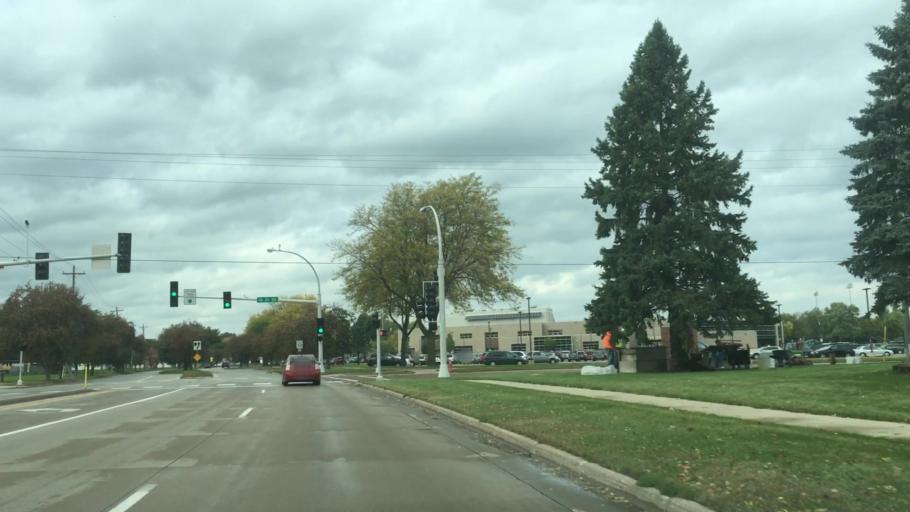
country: US
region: Minnesota
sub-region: Olmsted County
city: Rochester
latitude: 44.0002
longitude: -92.4457
